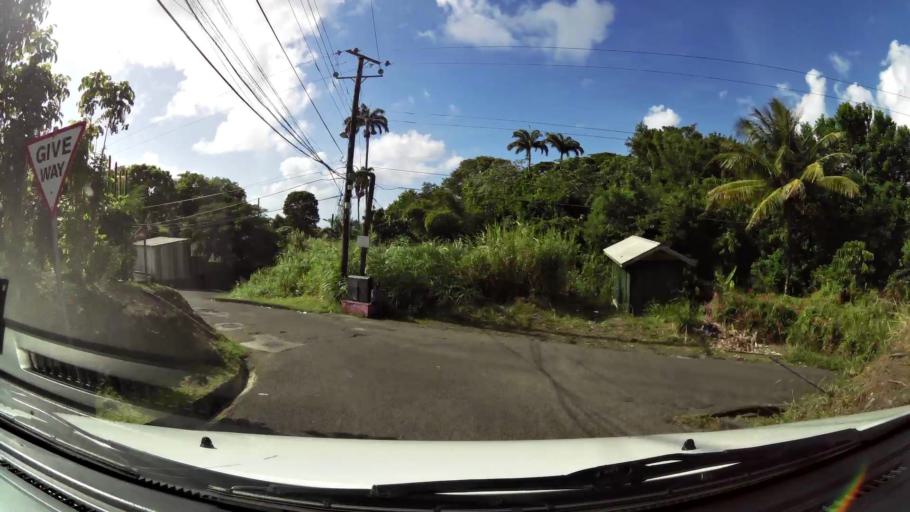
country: LC
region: Castries Quarter
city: Bisee
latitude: 14.0138
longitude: -60.9804
